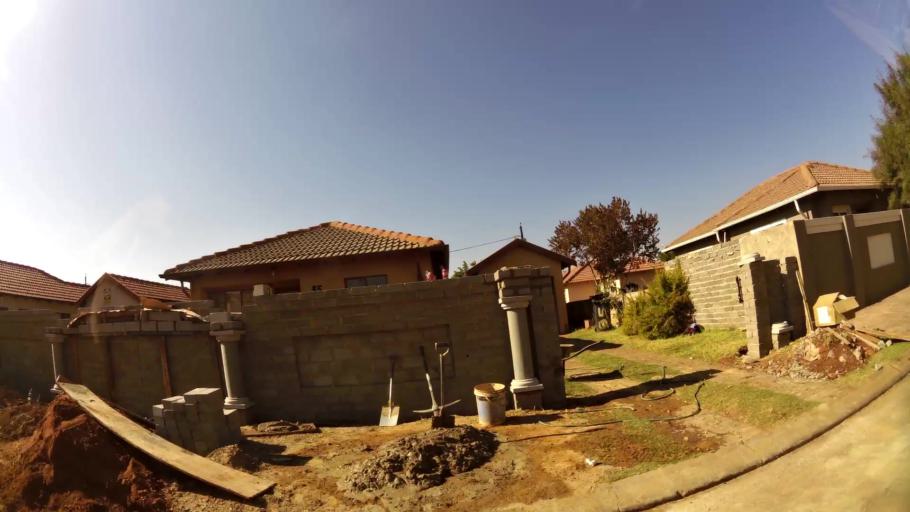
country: ZA
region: North-West
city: Ga-Rankuwa
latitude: -25.6382
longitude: 28.0877
